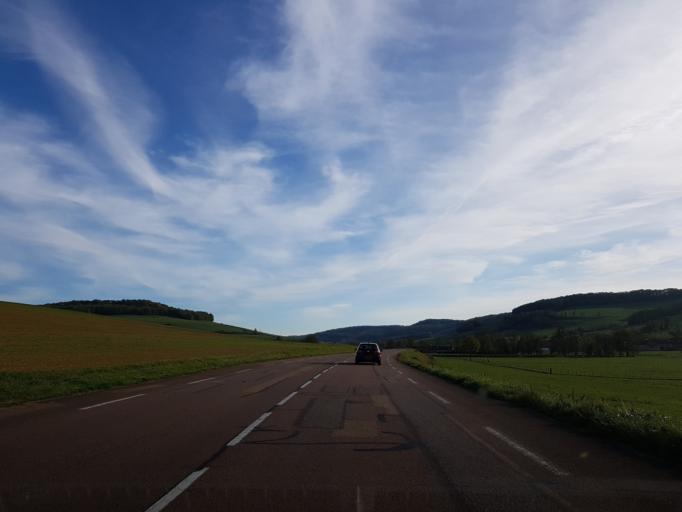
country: FR
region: Bourgogne
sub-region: Departement de la Cote-d'Or
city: Vitteaux
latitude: 47.3502
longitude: 4.5756
